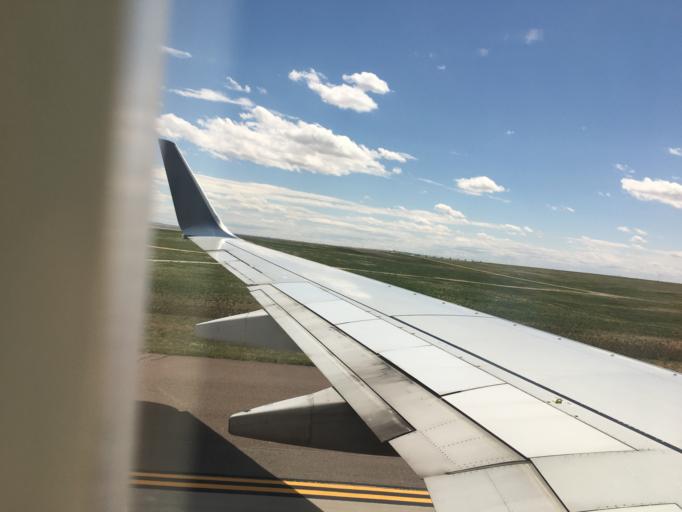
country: US
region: Colorado
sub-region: Weld County
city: Lochbuie
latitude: 39.8566
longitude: -104.6463
